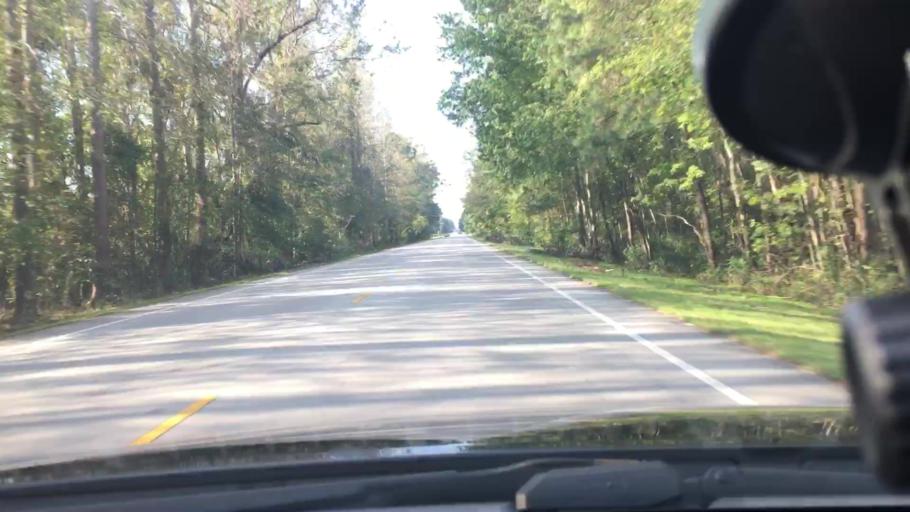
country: US
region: North Carolina
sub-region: Craven County
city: New Bern
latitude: 35.1916
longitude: -77.0526
